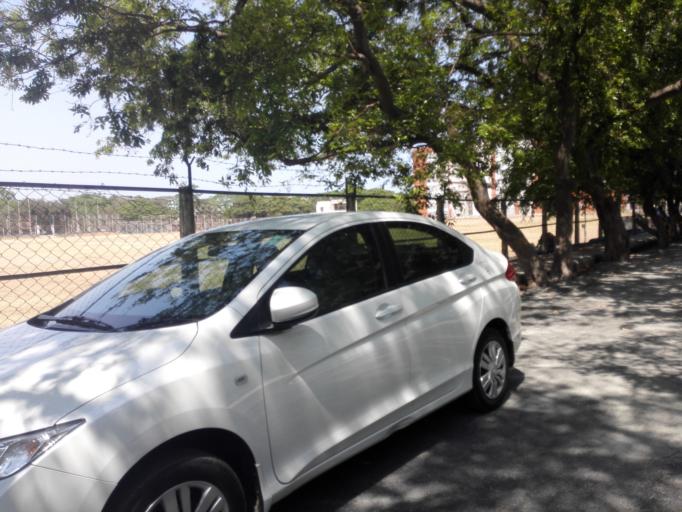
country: IN
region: Tamil Nadu
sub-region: Chennai
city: Gandhi Nagar
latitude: 13.0107
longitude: 80.2379
